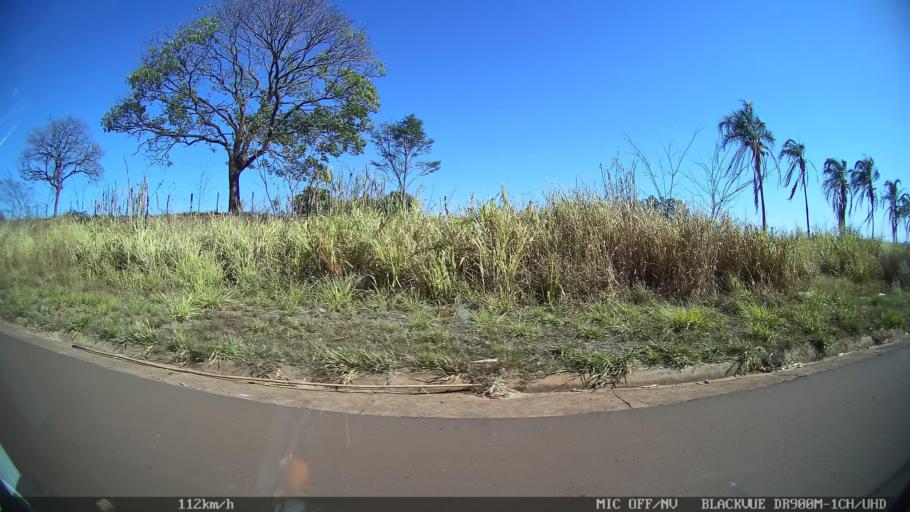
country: BR
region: Sao Paulo
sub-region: Olimpia
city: Olimpia
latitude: -20.6989
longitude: -48.8909
